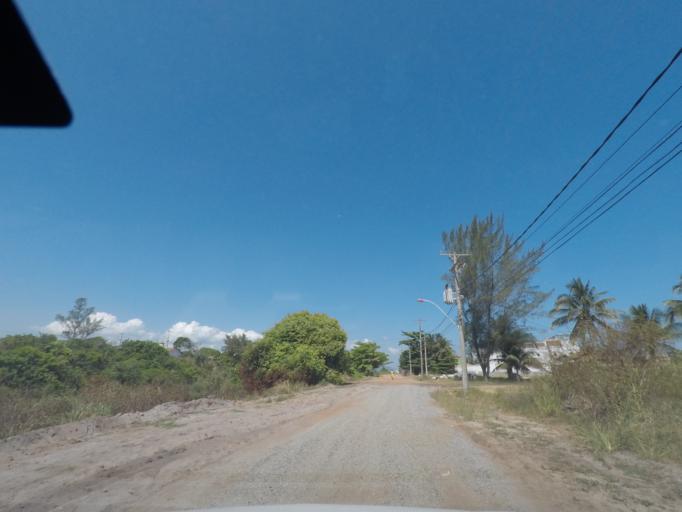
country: BR
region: Rio de Janeiro
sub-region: Marica
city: Marica
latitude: -22.9706
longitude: -42.9099
